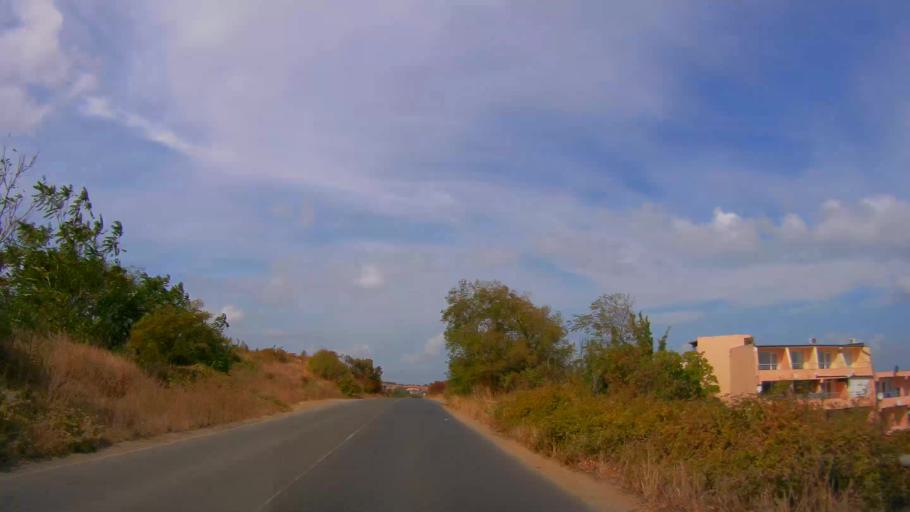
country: BG
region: Burgas
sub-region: Obshtina Sozopol
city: Sozopol
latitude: 42.4069
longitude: 27.7030
